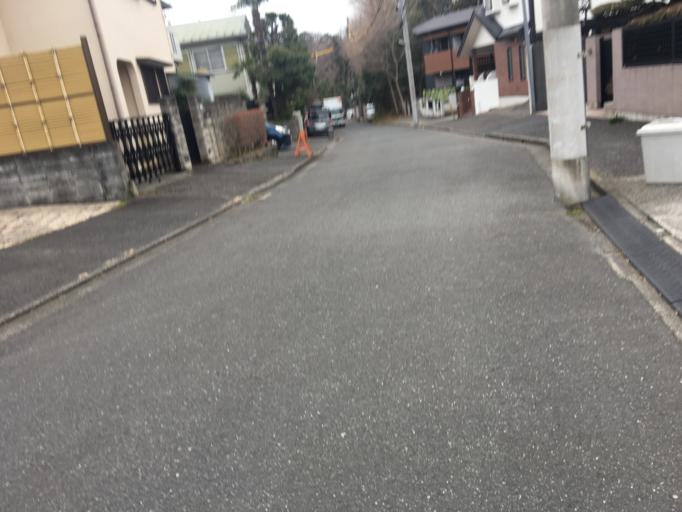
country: JP
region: Tokyo
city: Musashino
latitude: 35.6986
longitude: 139.5757
